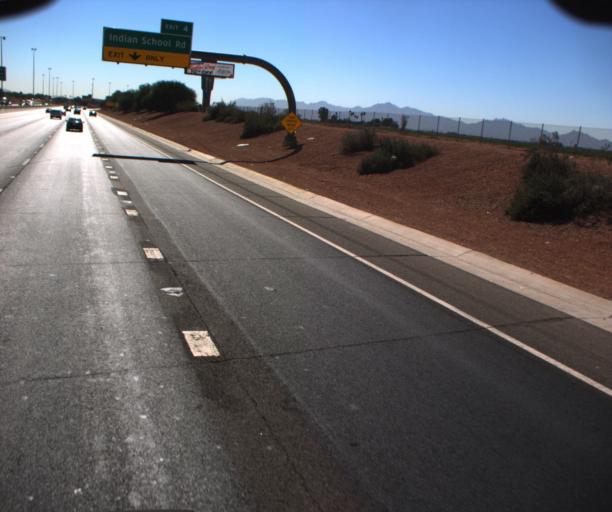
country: US
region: Arizona
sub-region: Maricopa County
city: Tolleson
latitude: 33.5020
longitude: -112.2679
